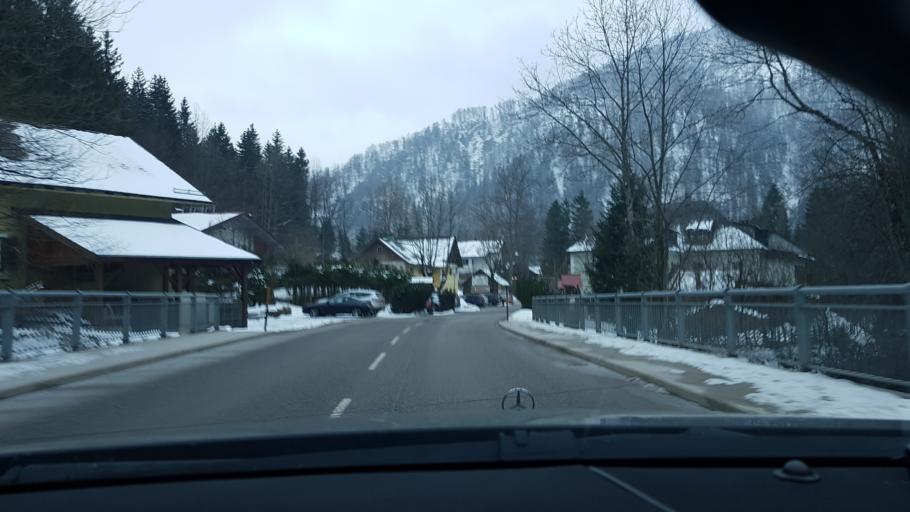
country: AT
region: Lower Austria
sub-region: Politischer Bezirk Scheibbs
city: Gaming
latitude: 47.8630
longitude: 15.1127
